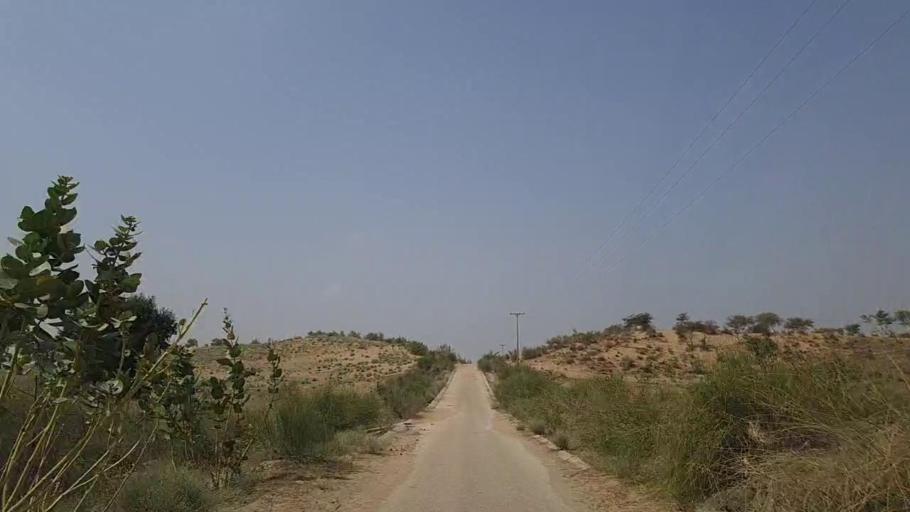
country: PK
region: Sindh
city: Mithi
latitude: 24.7716
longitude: 69.8885
